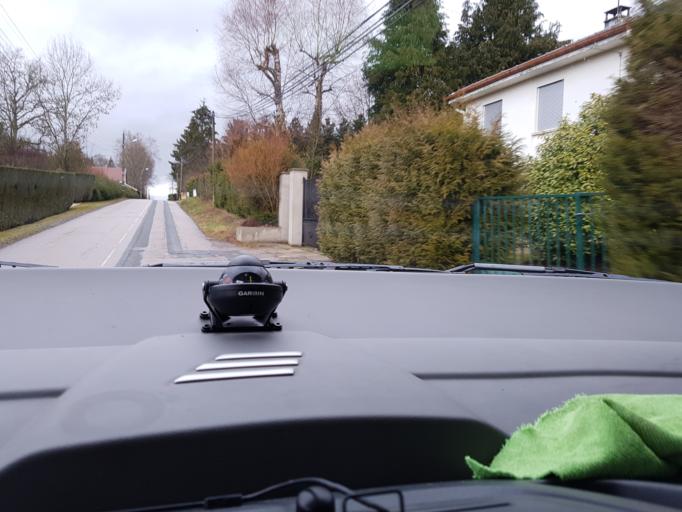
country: FR
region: Lorraine
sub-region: Departement des Vosges
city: Saint-Michel-sur-Meurthe
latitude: 48.3394
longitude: 6.8958
